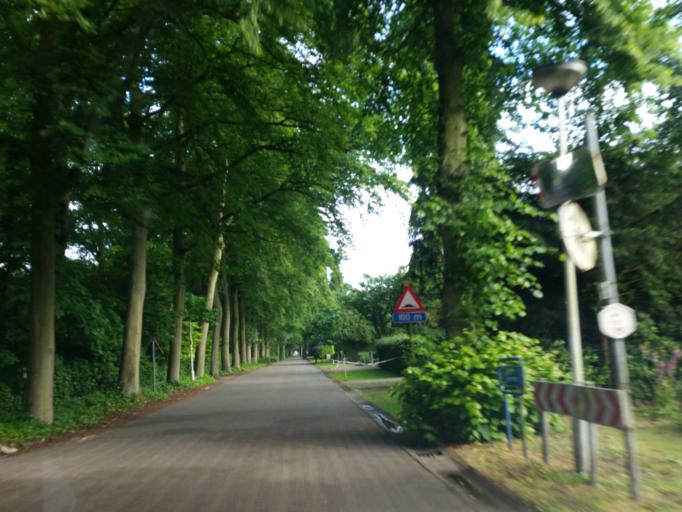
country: BE
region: Flanders
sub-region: Provincie Antwerpen
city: Kapellen
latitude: 51.3040
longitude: 4.4520
